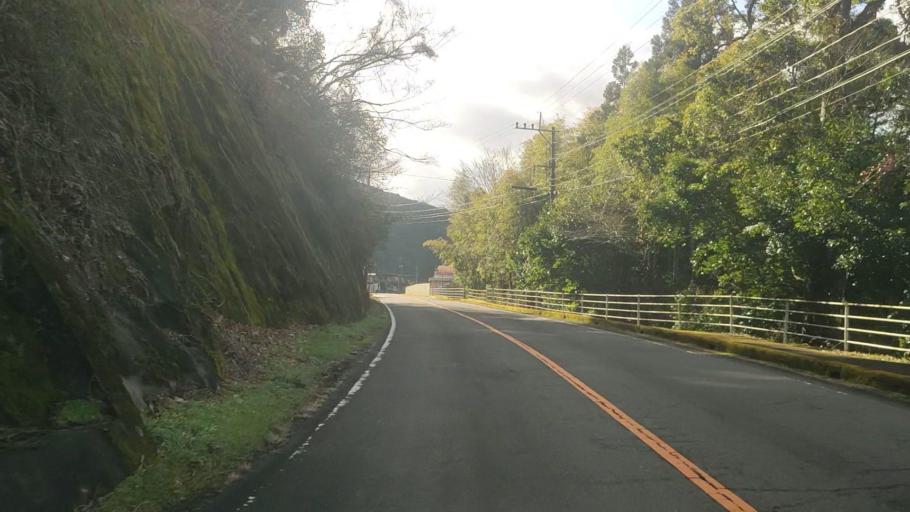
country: JP
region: Kumamoto
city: Hitoyoshi
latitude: 32.3097
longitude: 130.8477
